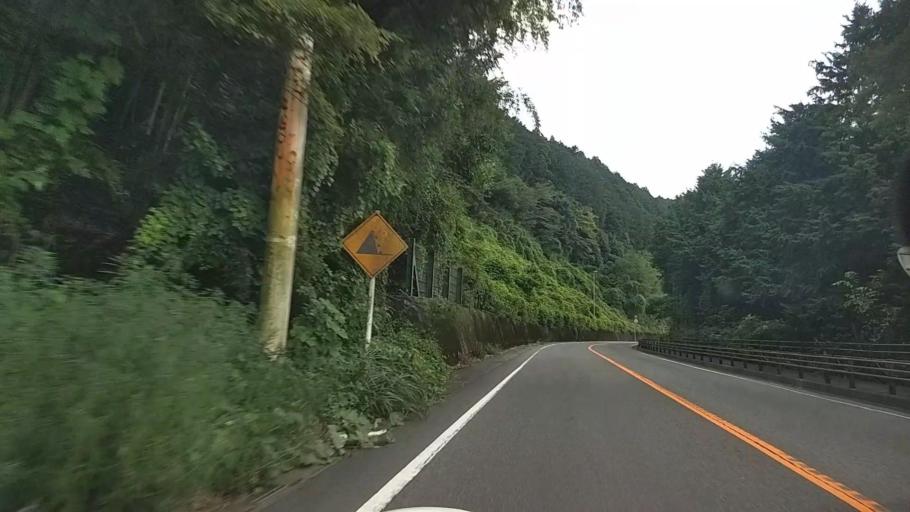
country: JP
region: Shizuoka
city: Fujinomiya
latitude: 35.2199
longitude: 138.5203
